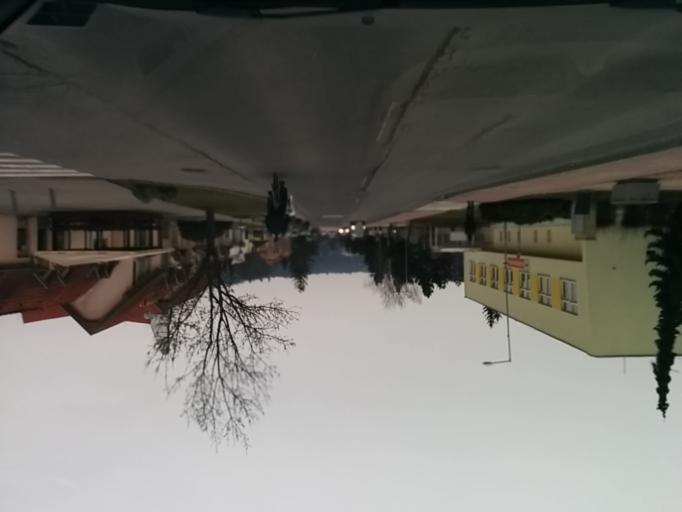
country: SK
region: Banskobystricky
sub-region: Okres Banska Bystrica
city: Zvolen
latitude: 48.6147
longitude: 19.1410
